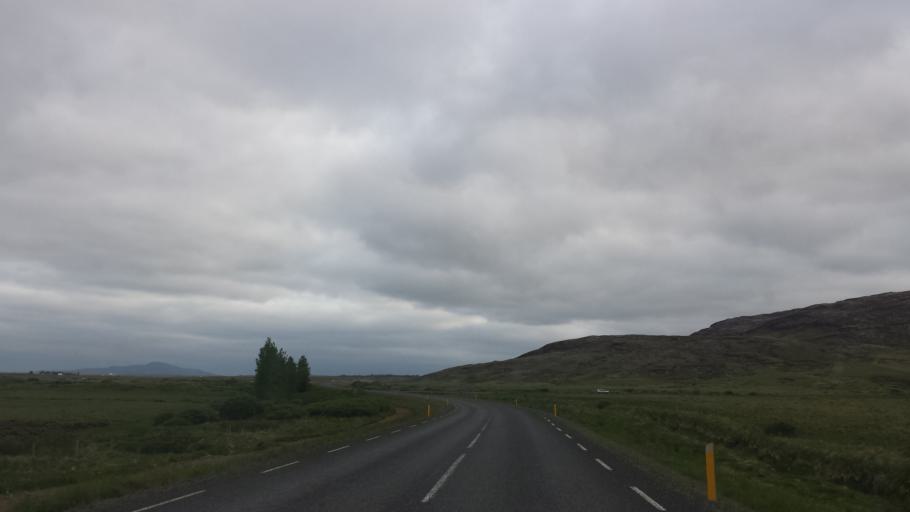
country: IS
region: South
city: Selfoss
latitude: 64.1397
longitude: -20.5707
